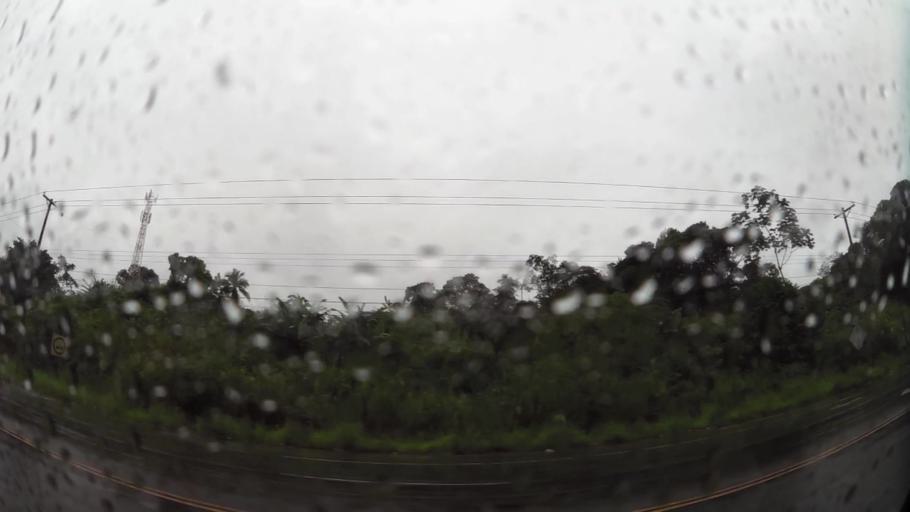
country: PA
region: Colon
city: Santa Rita Arriba
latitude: 9.3284
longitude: -79.8011
